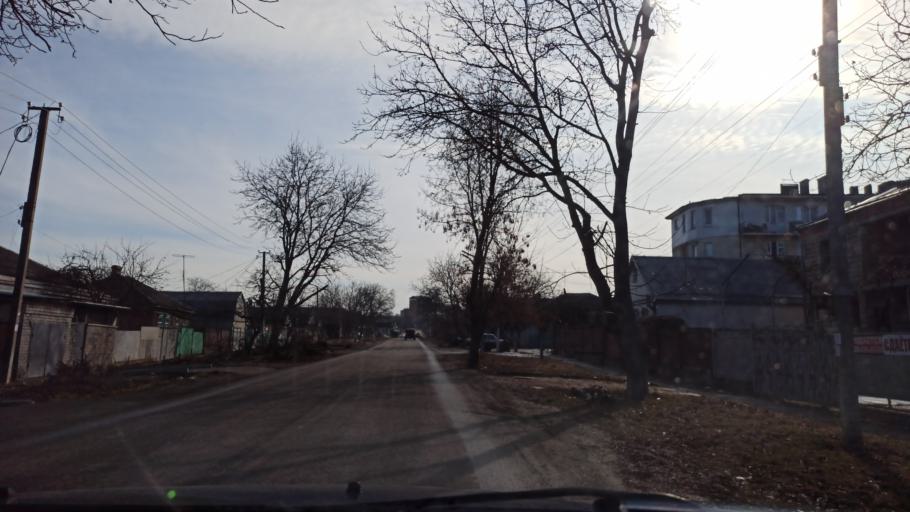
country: RU
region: Stavropol'skiy
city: Yessentuki
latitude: 44.0276
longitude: 42.8631
